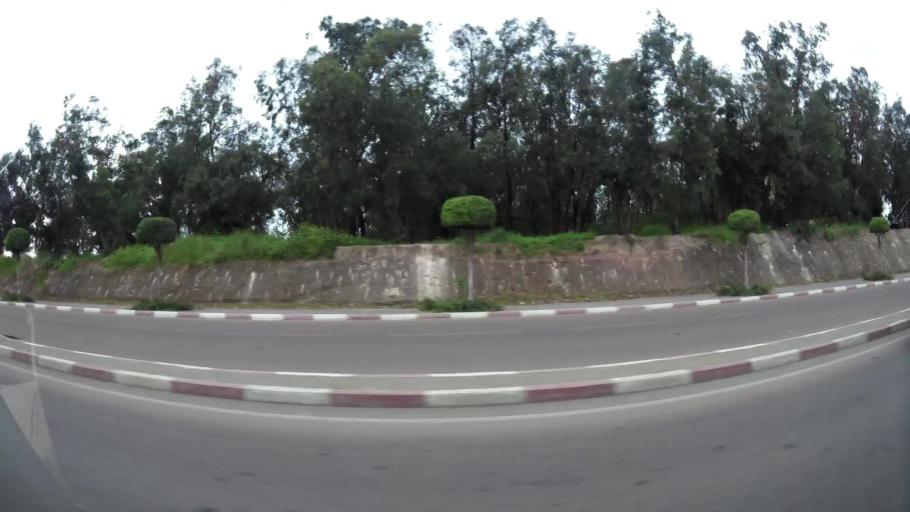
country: MA
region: Grand Casablanca
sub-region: Casablanca
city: Casablanca
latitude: 33.5248
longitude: -7.6354
